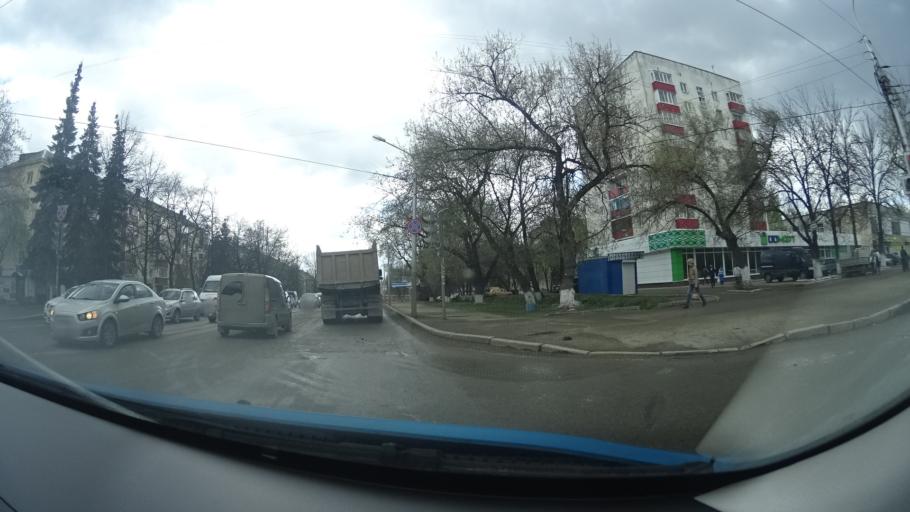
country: RU
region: Bashkortostan
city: Ufa
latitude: 54.8134
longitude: 56.0896
